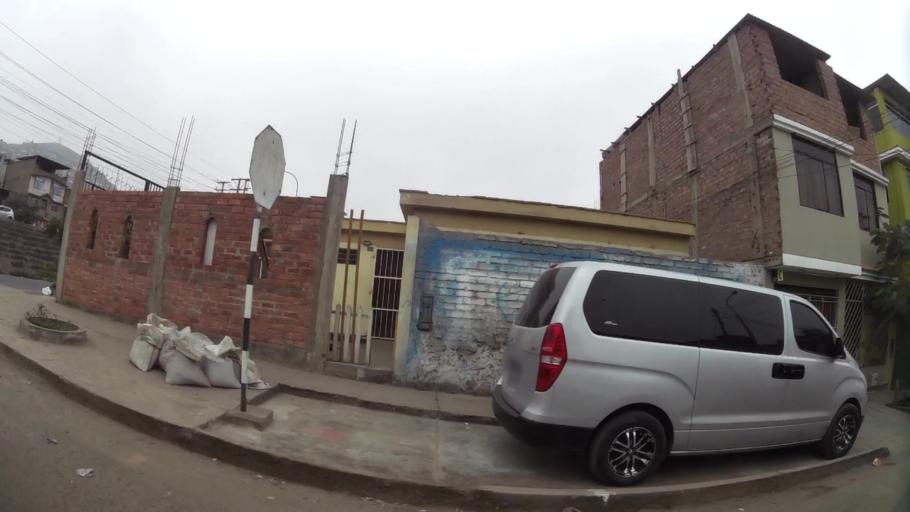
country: PE
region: Lima
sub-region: Lima
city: Surco
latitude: -12.1525
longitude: -76.9652
